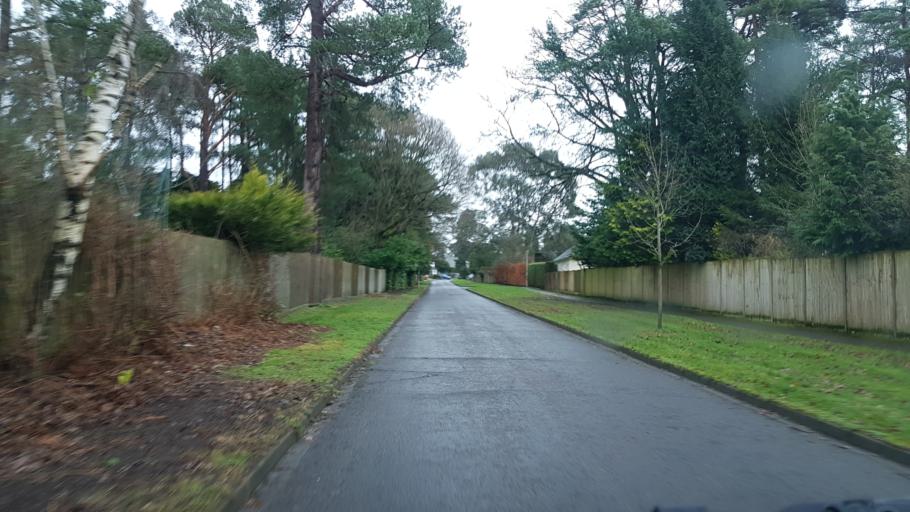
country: GB
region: England
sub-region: Surrey
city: Hindhead
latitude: 51.1059
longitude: -0.7511
